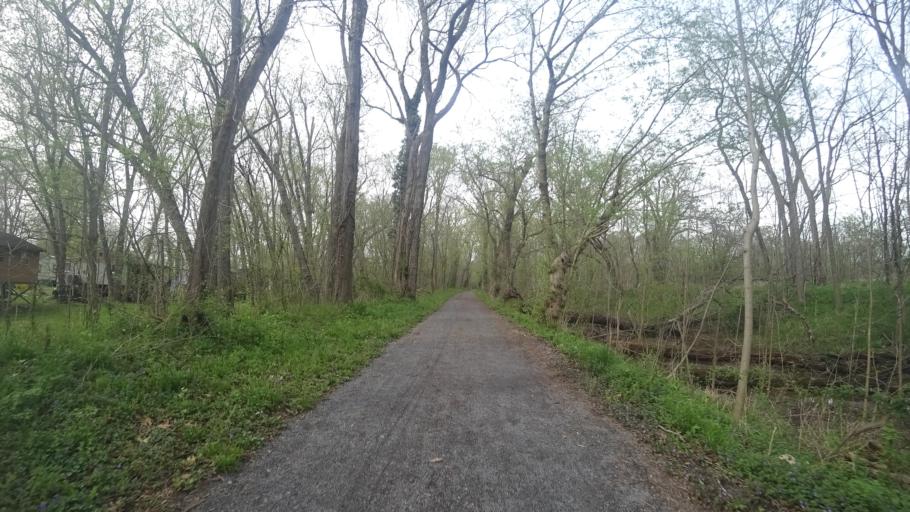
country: US
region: Virginia
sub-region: Loudoun County
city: Leesburg
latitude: 39.1505
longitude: -77.5179
